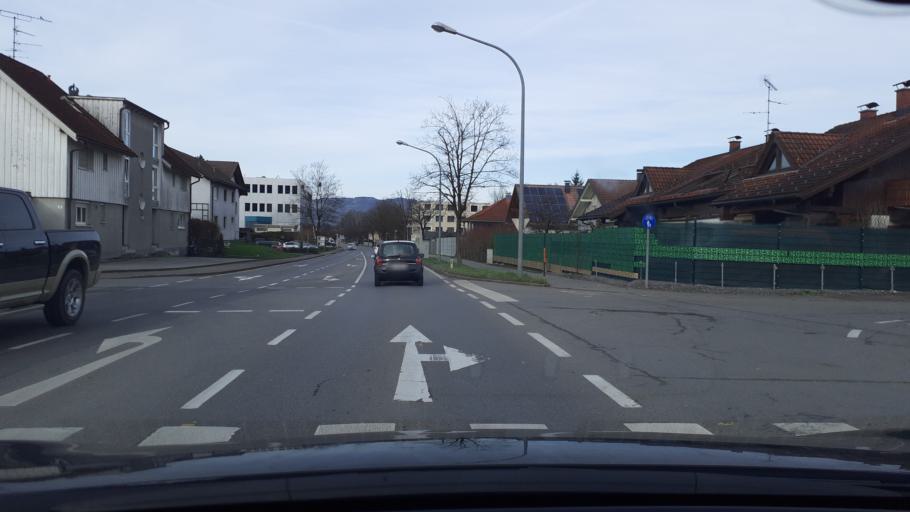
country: AT
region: Vorarlberg
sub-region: Politischer Bezirk Dornbirn
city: Hohenems
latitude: 47.3700
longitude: 9.6848
